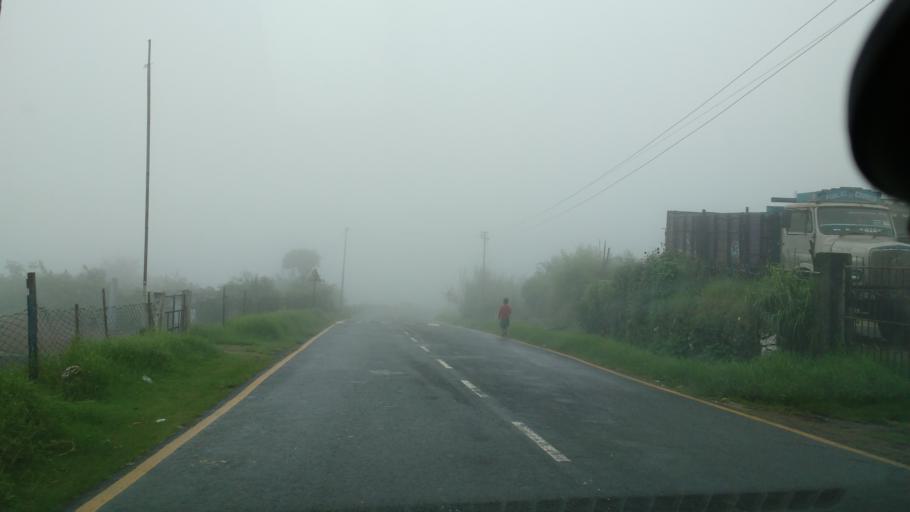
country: IN
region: Meghalaya
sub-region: East Khasi Hills
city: Cherrapunji
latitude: 25.3434
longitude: 91.7373
